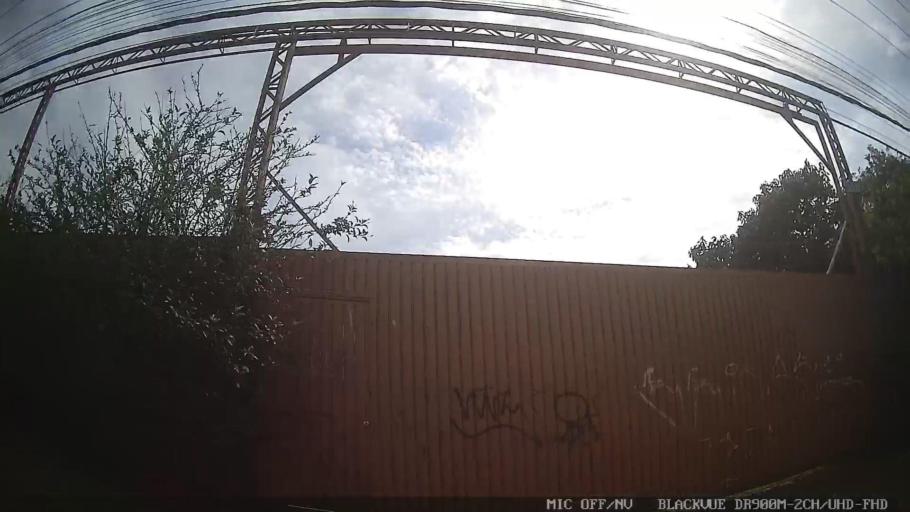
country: BR
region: Sao Paulo
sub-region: Itaquaquecetuba
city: Itaquaquecetuba
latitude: -23.4803
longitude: -46.3203
